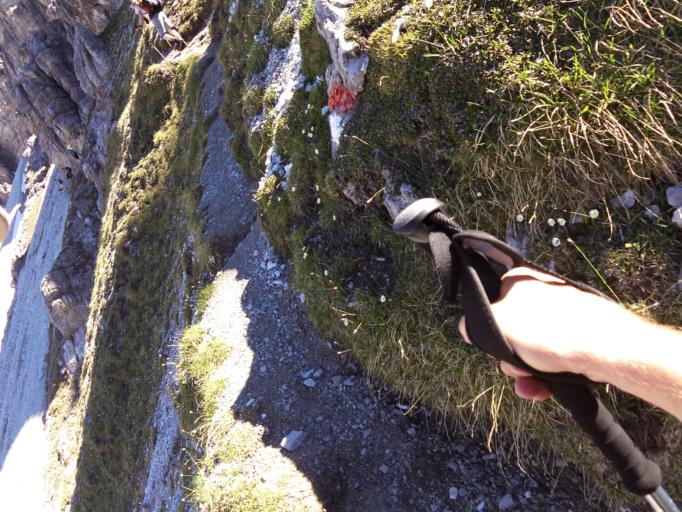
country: AT
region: Tyrol
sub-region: Politischer Bezirk Innsbruck Land
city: Neustift im Stubaital
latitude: 47.1401
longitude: 11.2748
